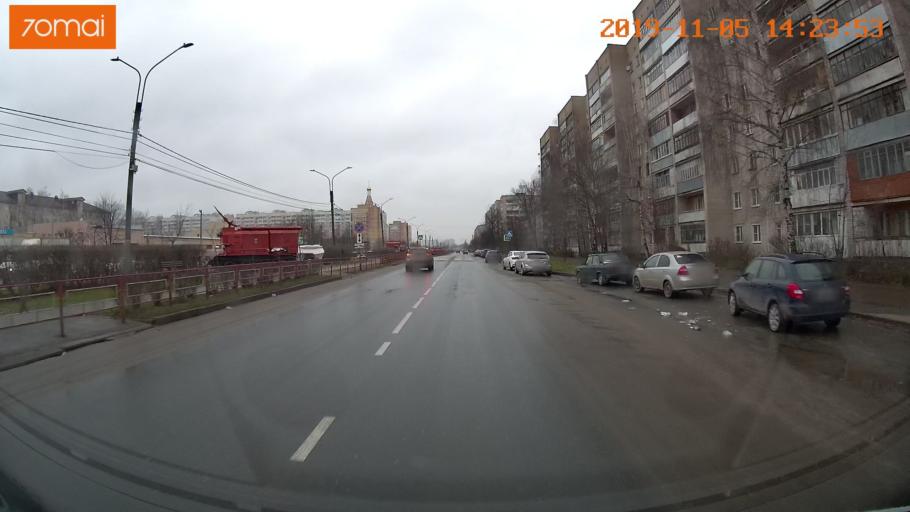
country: RU
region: Ivanovo
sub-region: Gorod Ivanovo
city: Ivanovo
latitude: 56.9658
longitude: 41.0013
